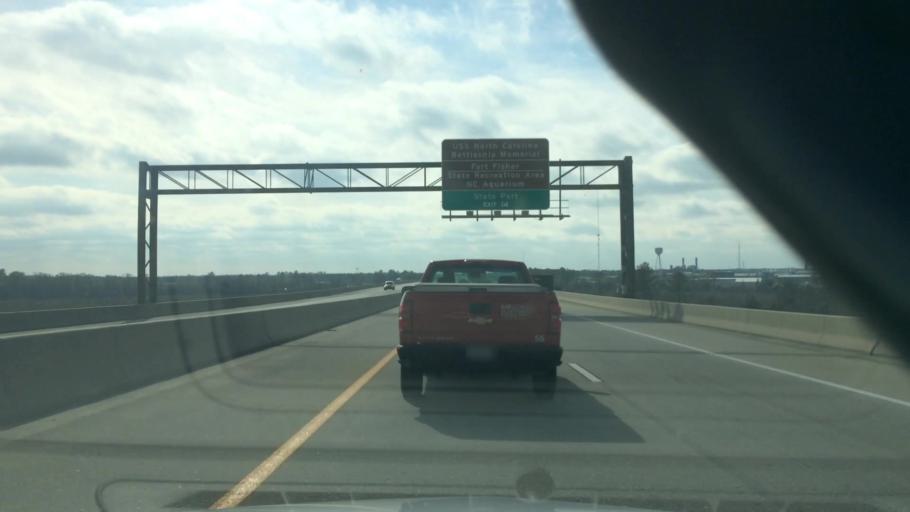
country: US
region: North Carolina
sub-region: New Hanover County
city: Wrightsboro
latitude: 34.2959
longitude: -77.9624
